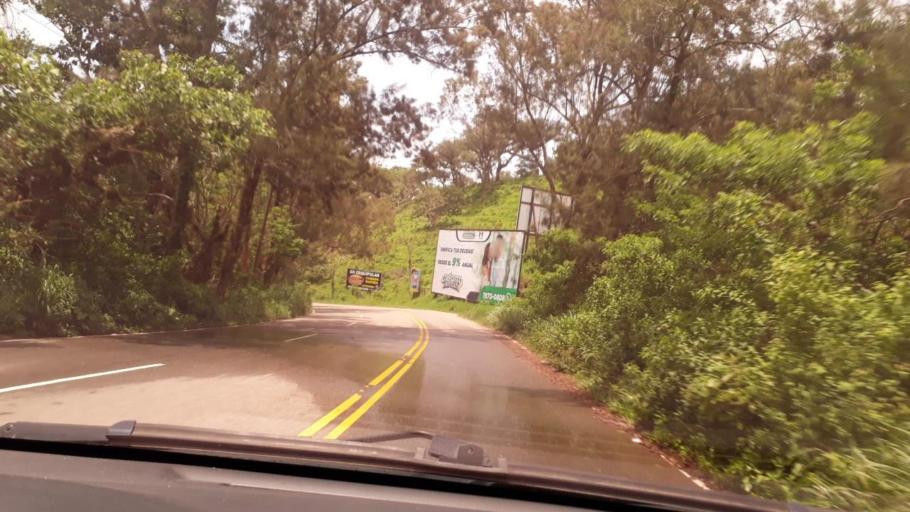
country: GT
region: Chiquimula
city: Esquipulas
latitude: 14.5507
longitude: -89.3900
